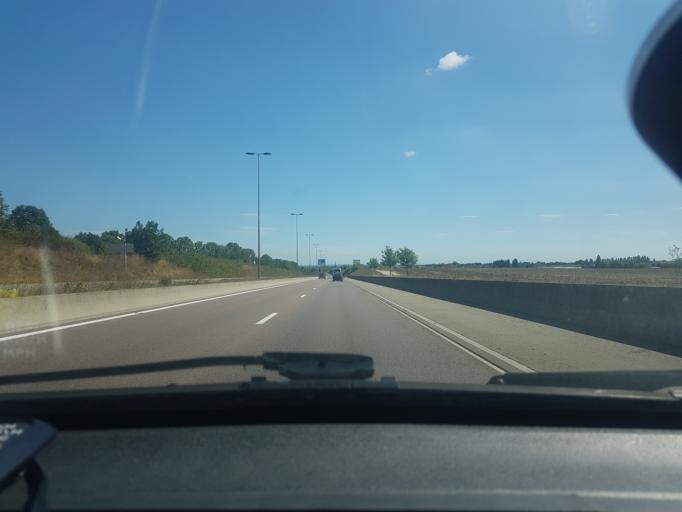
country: FR
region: Bourgogne
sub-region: Departement de la Cote-d'Or
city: Saint-Apollinaire
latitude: 47.3248
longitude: 5.0865
